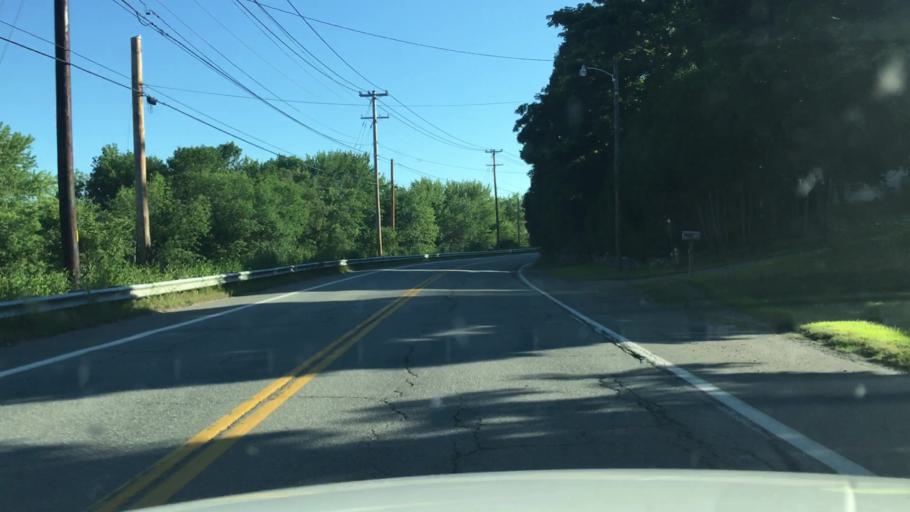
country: US
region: Maine
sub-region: Penobscot County
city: Veazie
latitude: 44.8176
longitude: -68.7311
